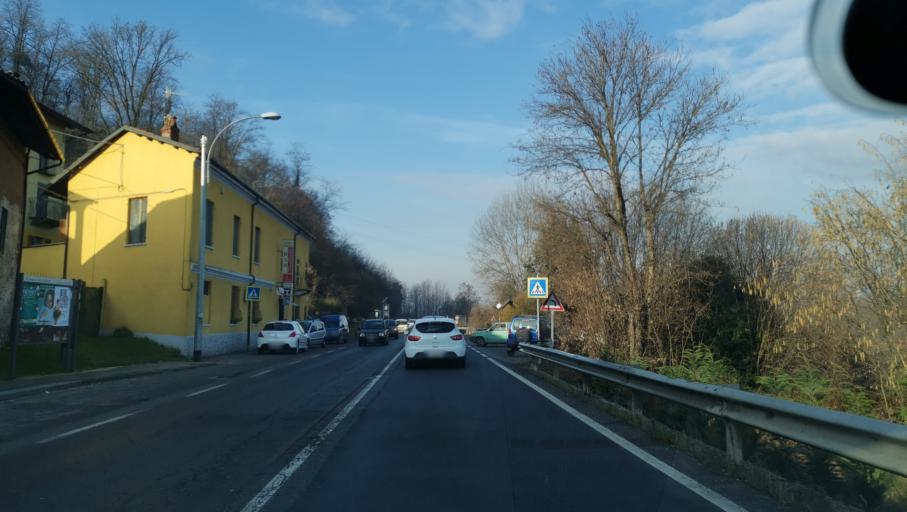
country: IT
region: Piedmont
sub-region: Provincia di Torino
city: Chivasso
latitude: 45.1768
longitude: 7.9106
